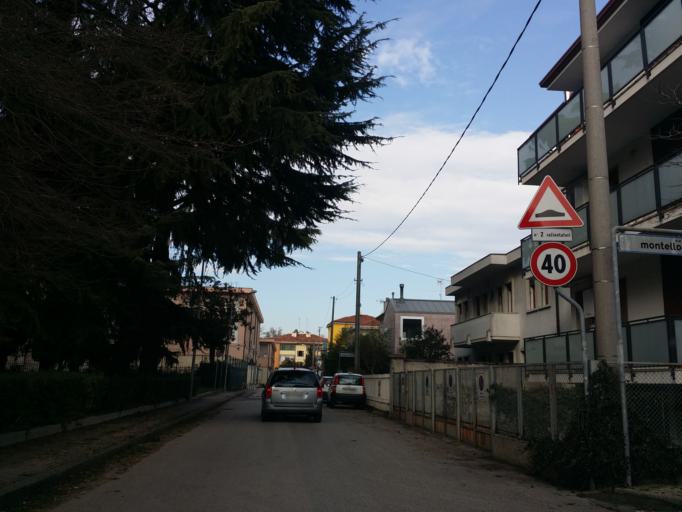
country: IT
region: Veneto
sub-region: Provincia di Padova
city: Padova
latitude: 45.4080
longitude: 11.8606
